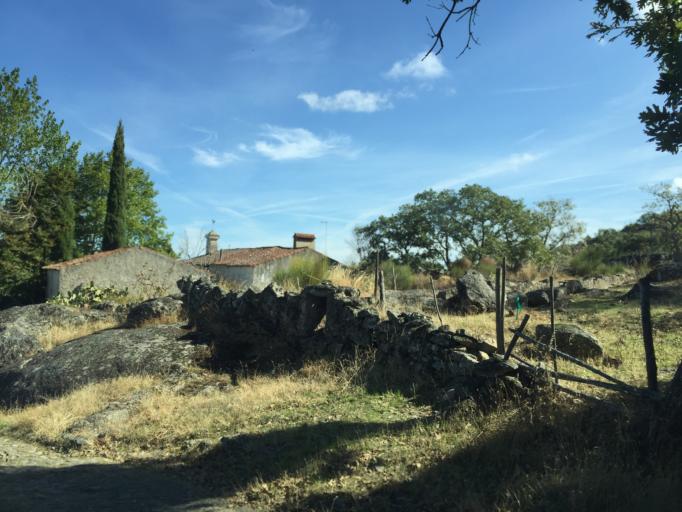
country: PT
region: Portalegre
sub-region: Marvao
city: Marvao
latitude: 39.3994
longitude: -7.3678
